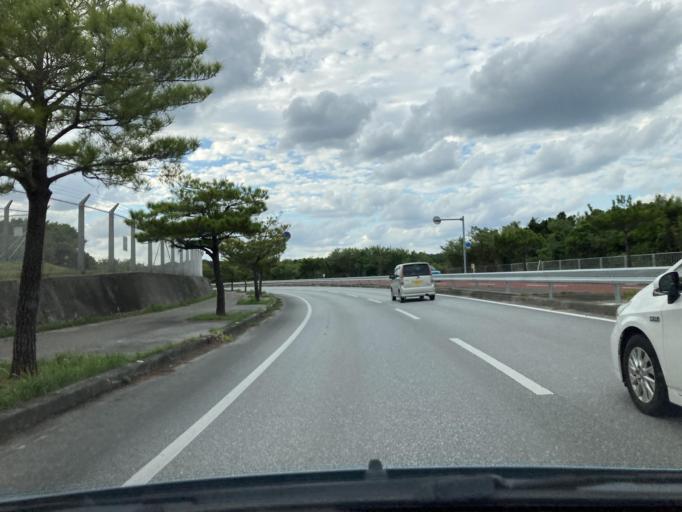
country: JP
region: Okinawa
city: Okinawa
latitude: 26.3685
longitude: 127.7854
